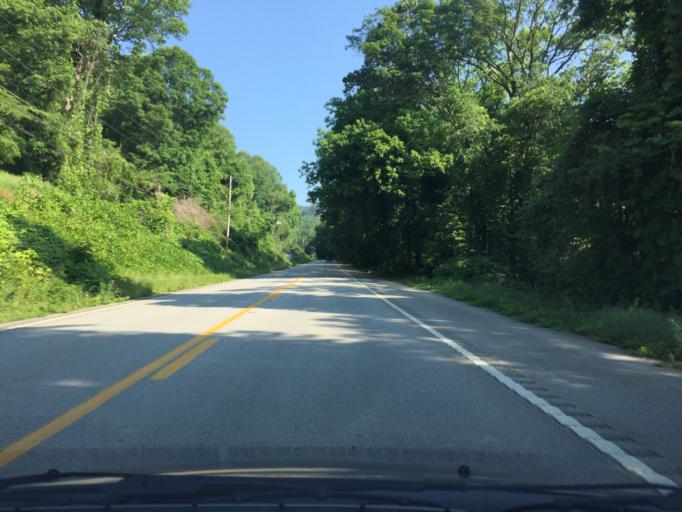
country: US
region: Tennessee
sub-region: Hamilton County
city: Lookout Mountain
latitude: 35.0296
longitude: -85.4061
